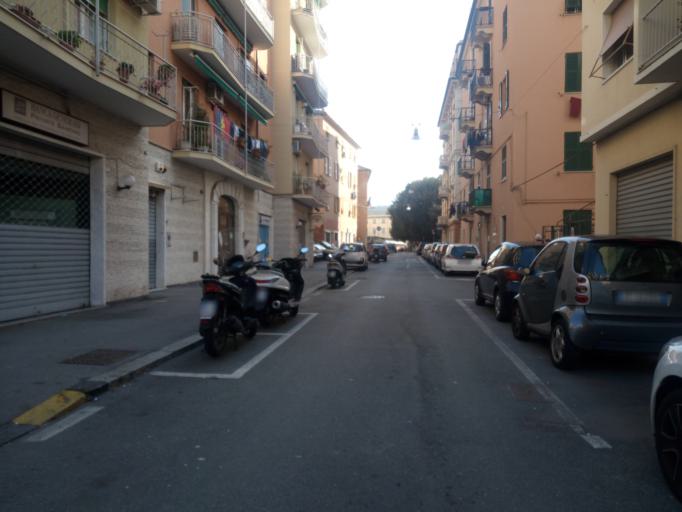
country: IT
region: Liguria
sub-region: Provincia di Genova
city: Mele
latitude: 44.4276
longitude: 8.7832
